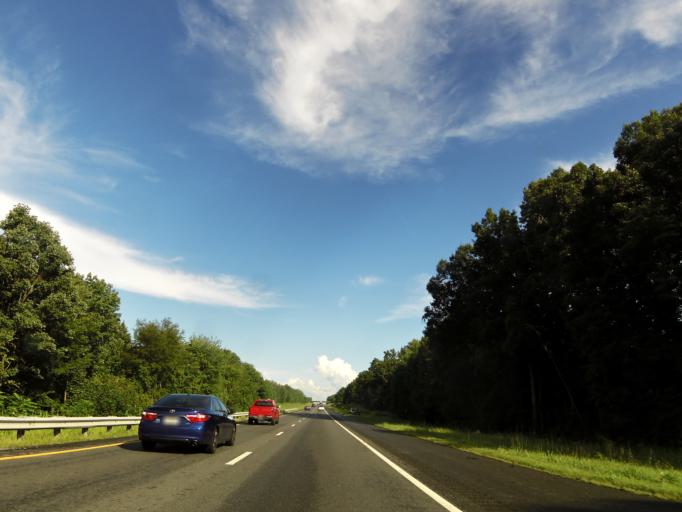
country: US
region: Tennessee
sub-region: Cheatham County
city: Pleasant View
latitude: 36.4821
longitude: -87.1519
